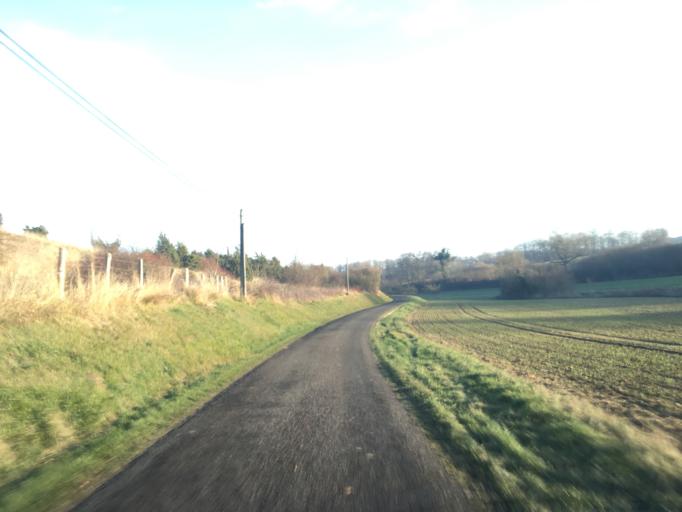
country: FR
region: Haute-Normandie
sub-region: Departement de l'Eure
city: Menilles
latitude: 49.0483
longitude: 1.2822
